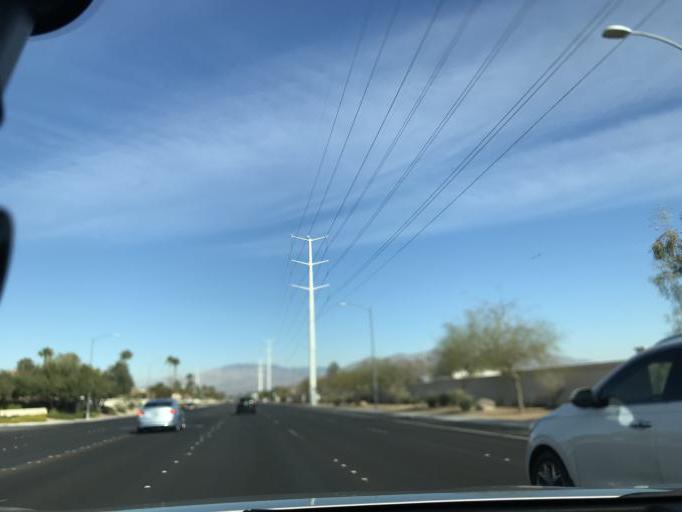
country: US
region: Nevada
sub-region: Clark County
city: Spring Valley
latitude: 36.2132
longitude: -115.2605
